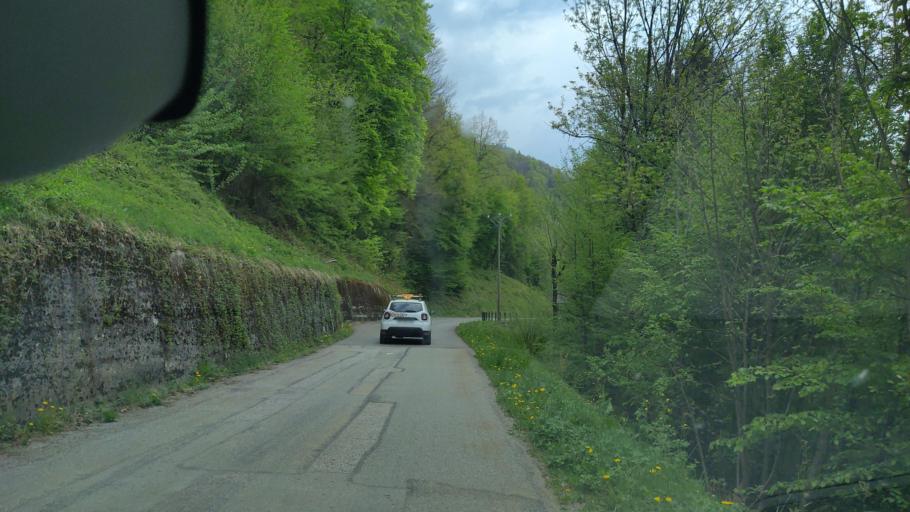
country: FR
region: Rhone-Alpes
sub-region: Departement de la Savoie
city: Marthod
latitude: 45.7369
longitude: 6.4320
